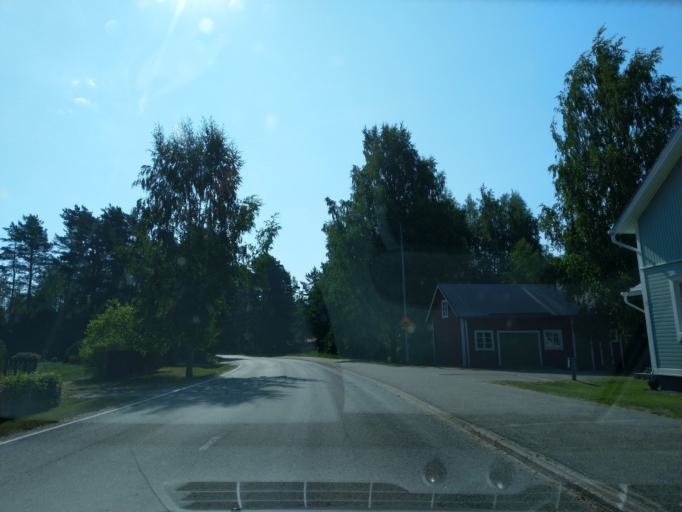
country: FI
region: Satakunta
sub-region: Pori
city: Noormarkku
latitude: 61.5884
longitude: 21.8896
